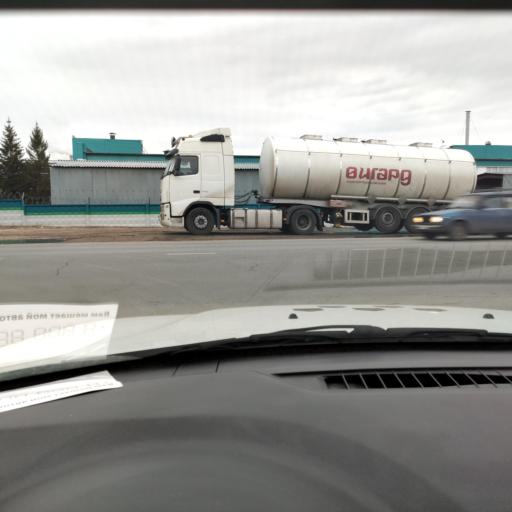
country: RU
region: Samara
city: Tol'yatti
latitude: 53.5333
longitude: 49.4490
